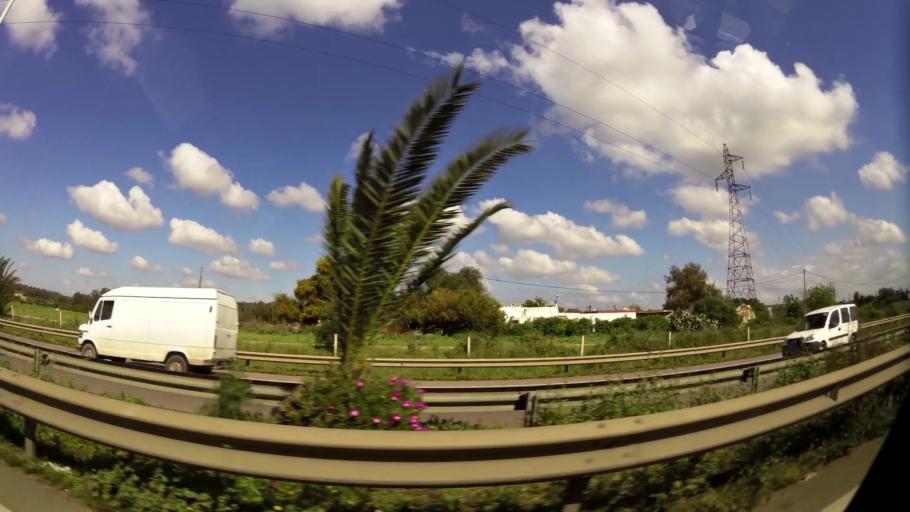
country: MA
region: Grand Casablanca
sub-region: Nouaceur
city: Bouskoura
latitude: 33.4576
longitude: -7.6335
